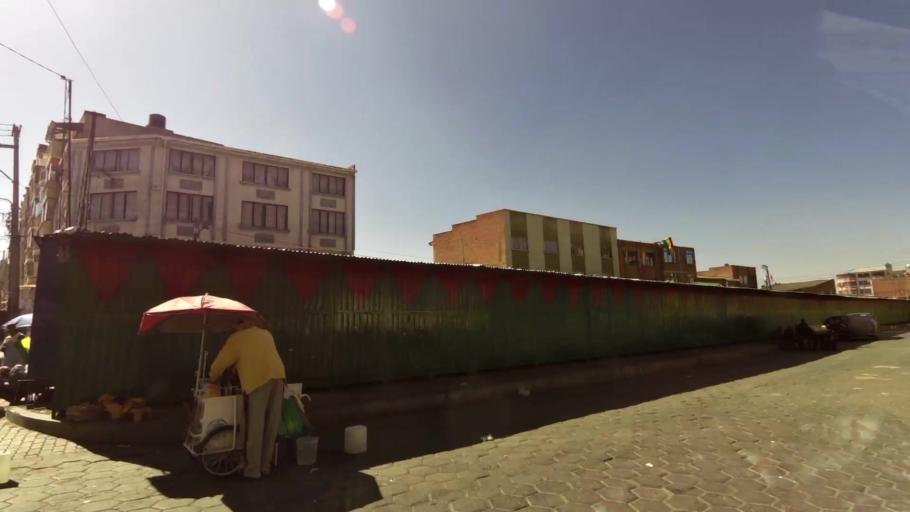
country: BO
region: La Paz
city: La Paz
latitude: -16.5112
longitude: -68.1614
